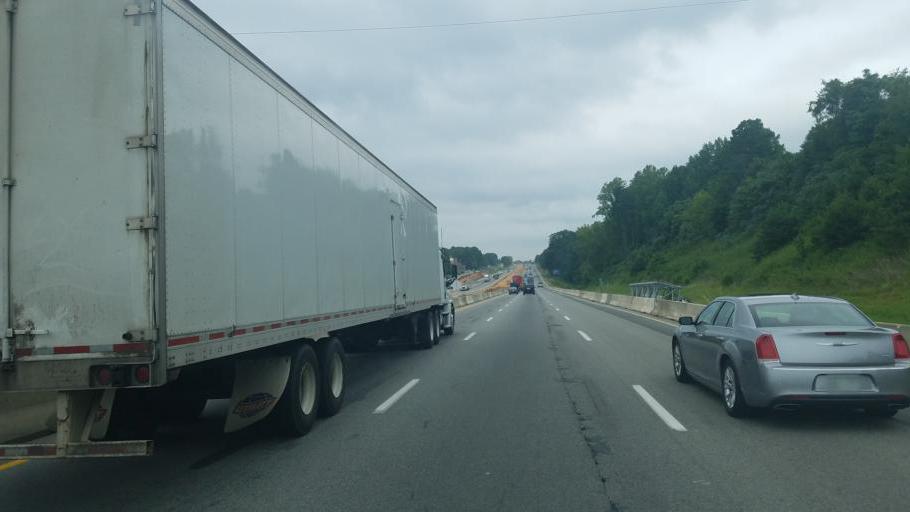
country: US
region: North Carolina
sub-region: Gaston County
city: Davidson
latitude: 35.5358
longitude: -80.8611
